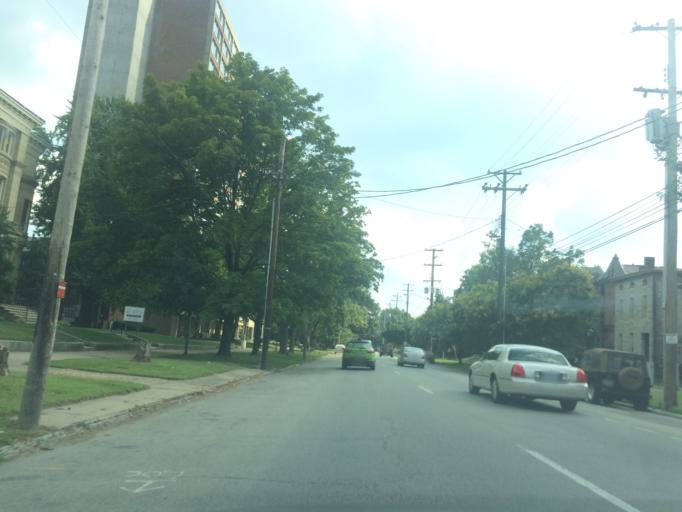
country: US
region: Kentucky
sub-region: Jefferson County
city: Louisville
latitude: 38.2346
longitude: -85.7587
